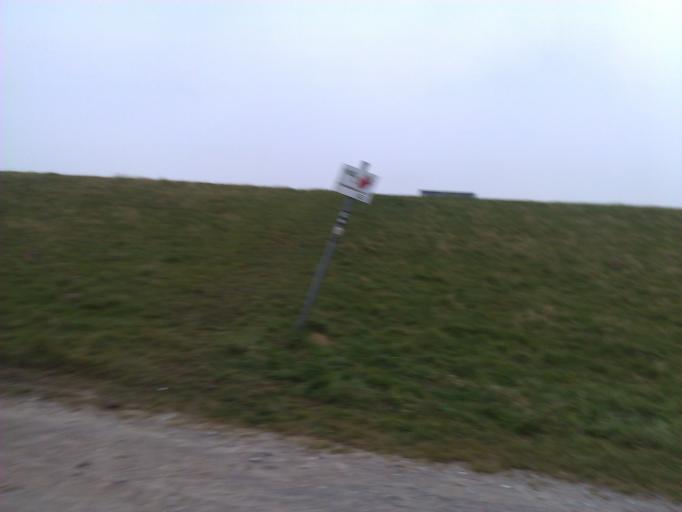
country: DE
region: North Rhine-Westphalia
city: Monheim am Rhein
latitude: 51.1111
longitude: 6.8698
